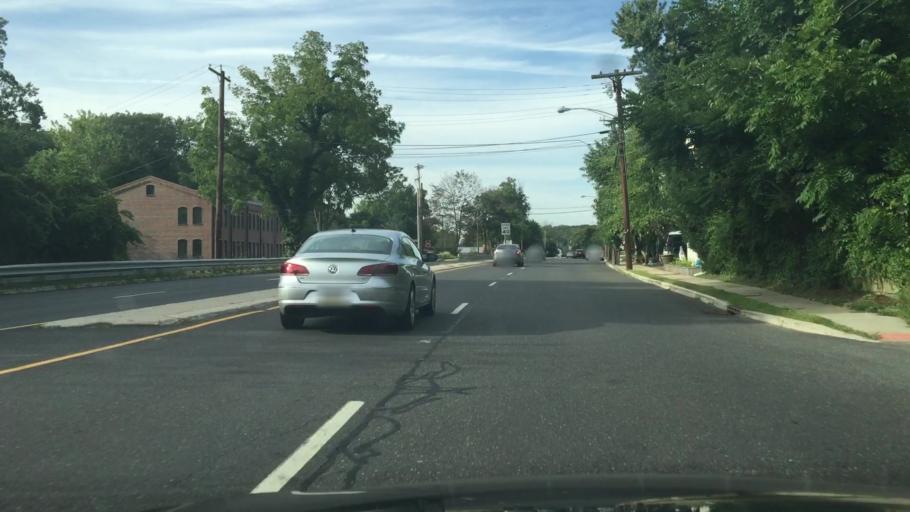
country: US
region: New Jersey
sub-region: Hunterdon County
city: Lambertville
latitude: 40.3585
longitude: -74.9427
